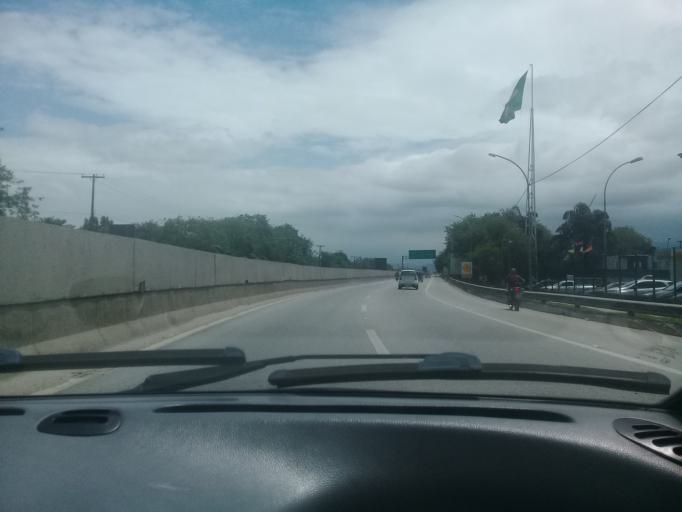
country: BR
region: Sao Paulo
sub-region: Guaruja
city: Guaruja
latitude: -23.9823
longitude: -46.2655
